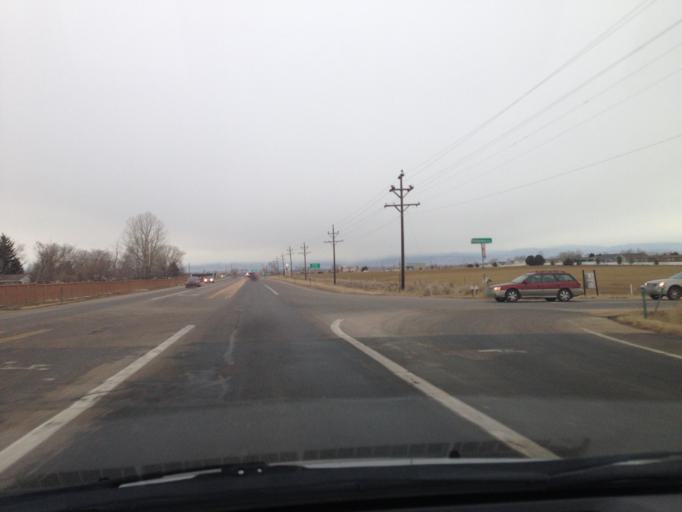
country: US
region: Colorado
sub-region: Weld County
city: Dacono
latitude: 40.0878
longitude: -104.9235
